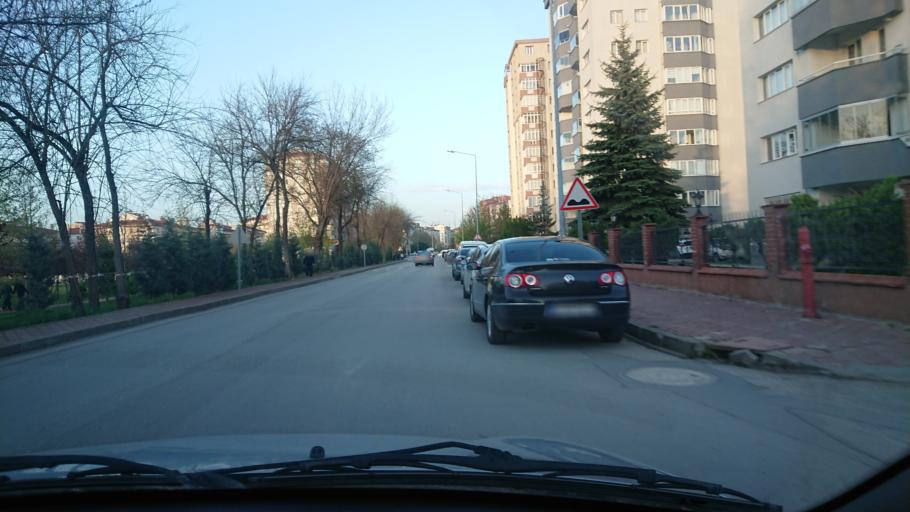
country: TR
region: Eskisehir
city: Eskisehir
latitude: 39.7638
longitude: 30.4959
